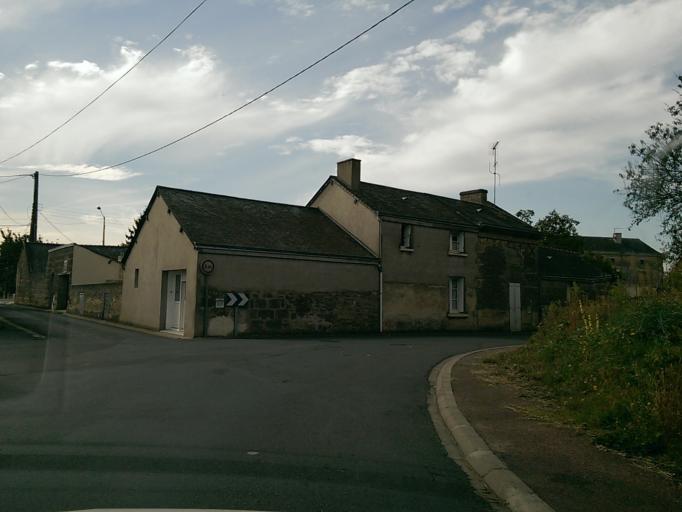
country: FR
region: Pays de la Loire
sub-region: Departement de Maine-et-Loire
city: Doue-la-Fontaine
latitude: 47.1964
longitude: -0.2637
